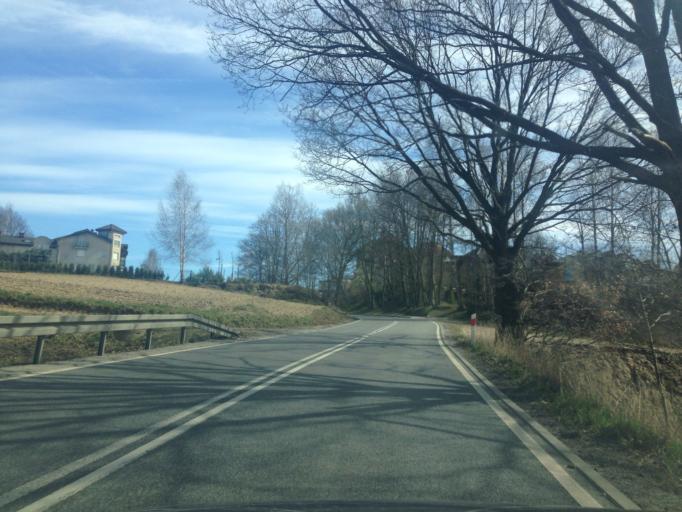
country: PL
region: Pomeranian Voivodeship
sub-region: Gdynia
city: Wielki Kack
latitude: 54.4759
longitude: 18.4611
